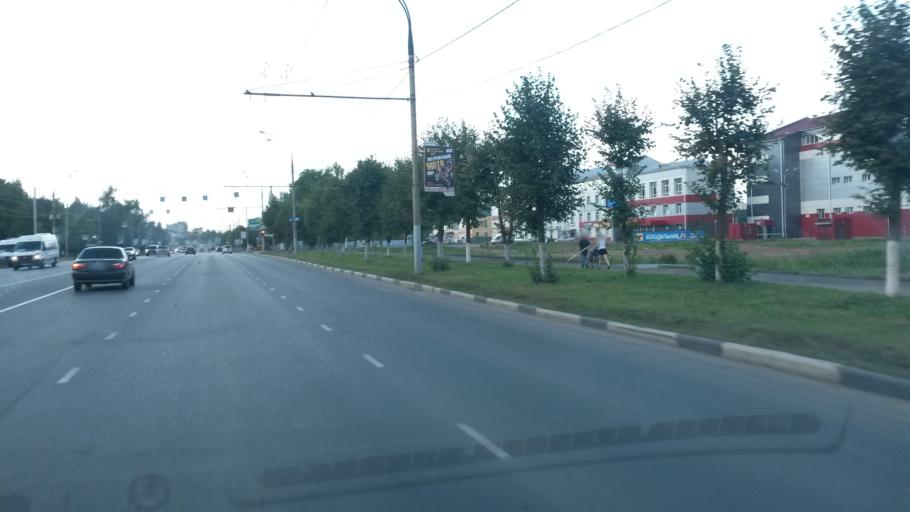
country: RU
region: Ivanovo
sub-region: Gorod Ivanovo
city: Ivanovo
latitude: 56.9602
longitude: 40.9740
